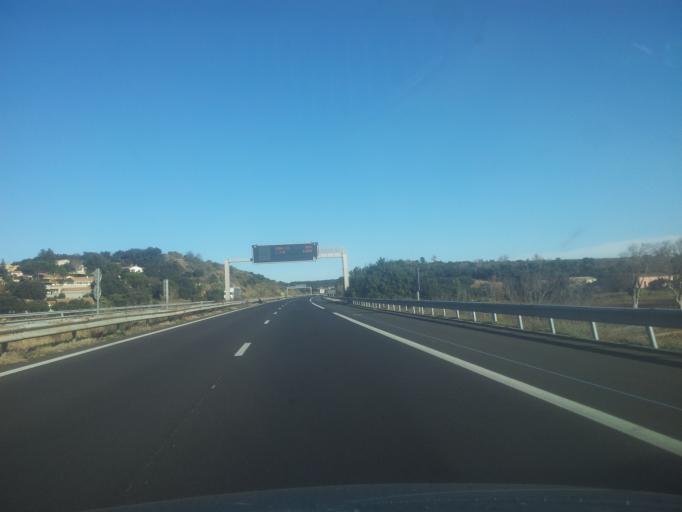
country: FR
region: Languedoc-Roussillon
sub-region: Departement du Gard
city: Tavel
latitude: 44.0093
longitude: 4.7132
